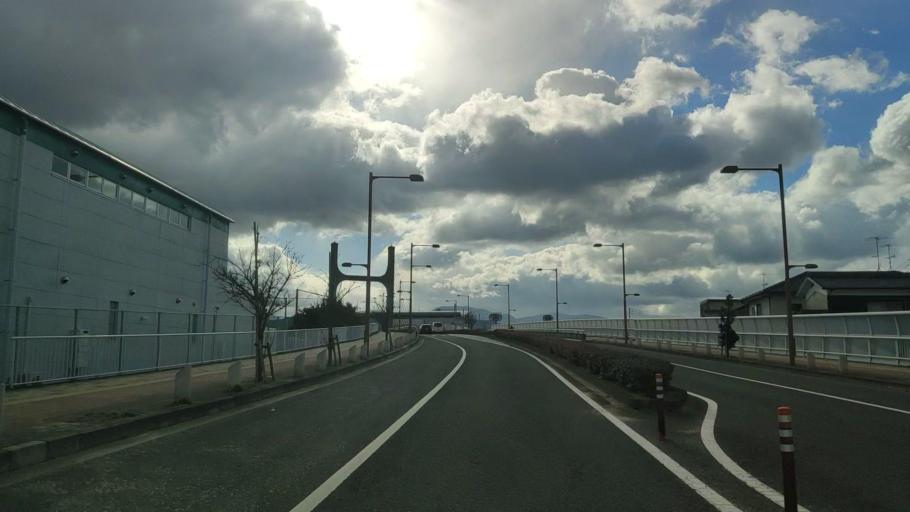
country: JP
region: Ehime
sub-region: Shikoku-chuo Shi
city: Matsuyama
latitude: 33.8125
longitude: 132.7411
